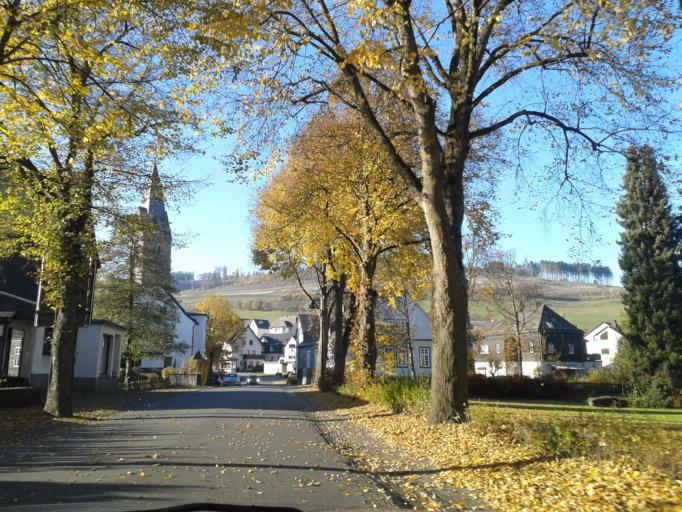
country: DE
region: North Rhine-Westphalia
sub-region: Regierungsbezirk Arnsberg
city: Bestwig
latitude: 51.3694
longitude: 8.4264
